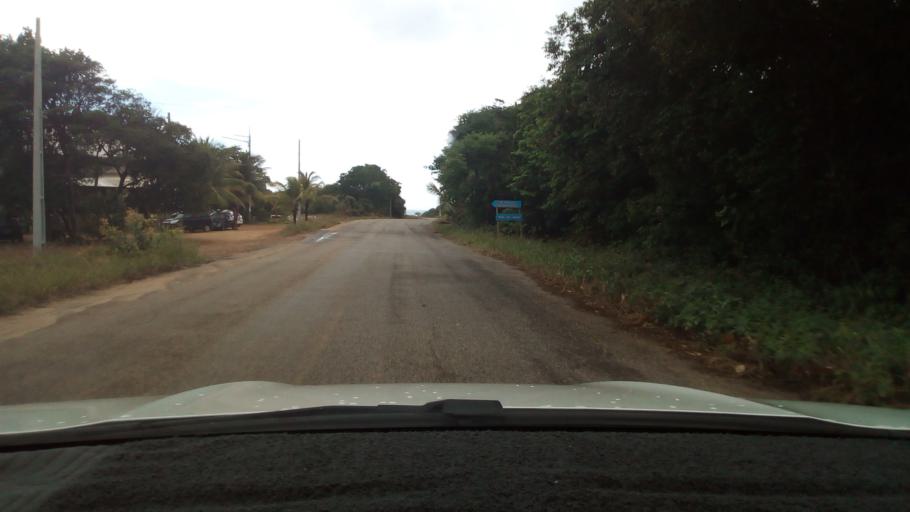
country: BR
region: Paraiba
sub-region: Pitimbu
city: Pitimbu
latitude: -7.3621
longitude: -34.8029
